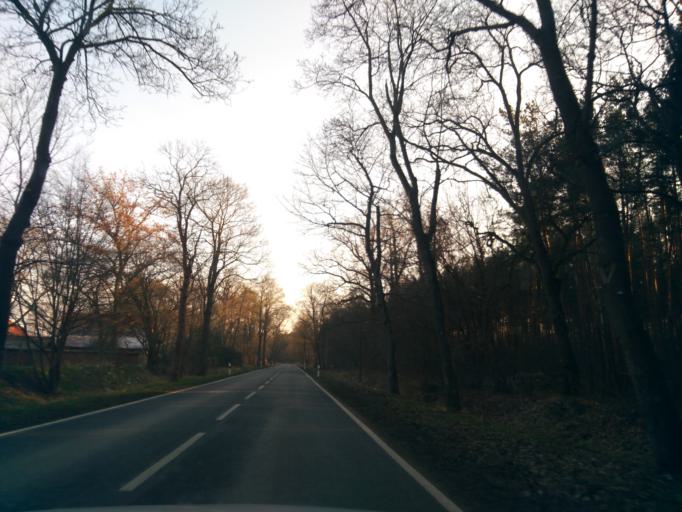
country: DE
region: Brandenburg
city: Brieselang
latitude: 52.6026
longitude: 13.0412
